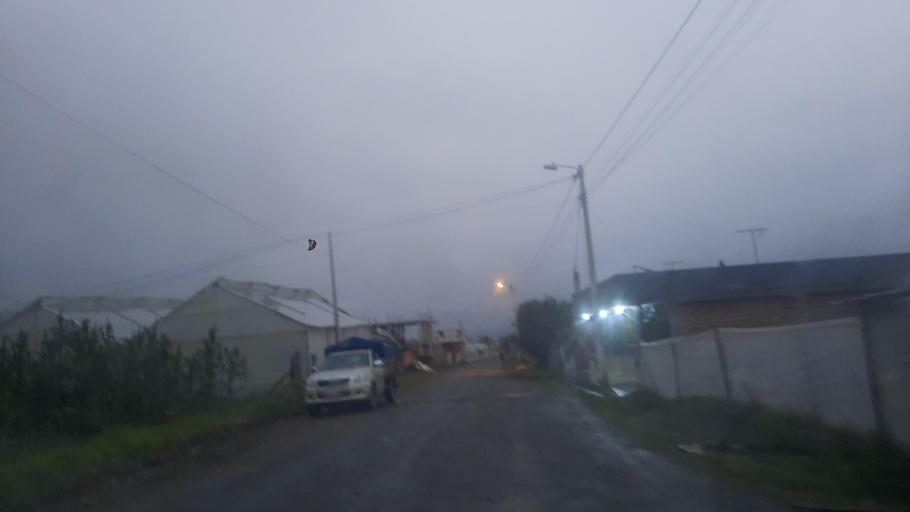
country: EC
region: Chimborazo
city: Riobamba
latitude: -1.6884
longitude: -78.6682
